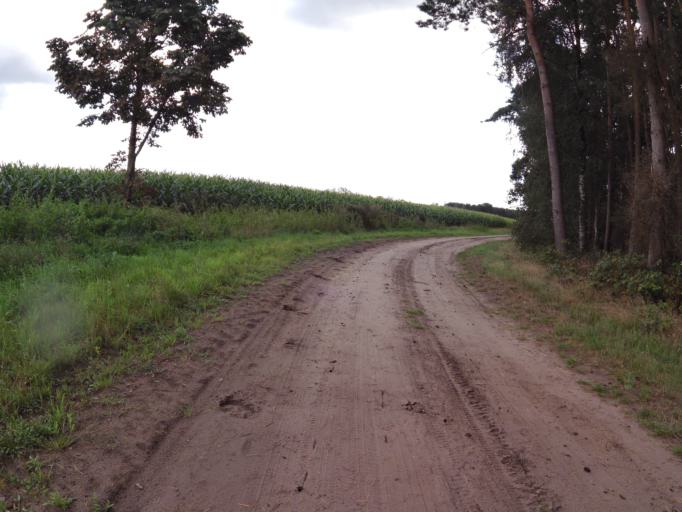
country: DE
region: Lower Saxony
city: Sandbostel
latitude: 53.3772
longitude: 9.1485
